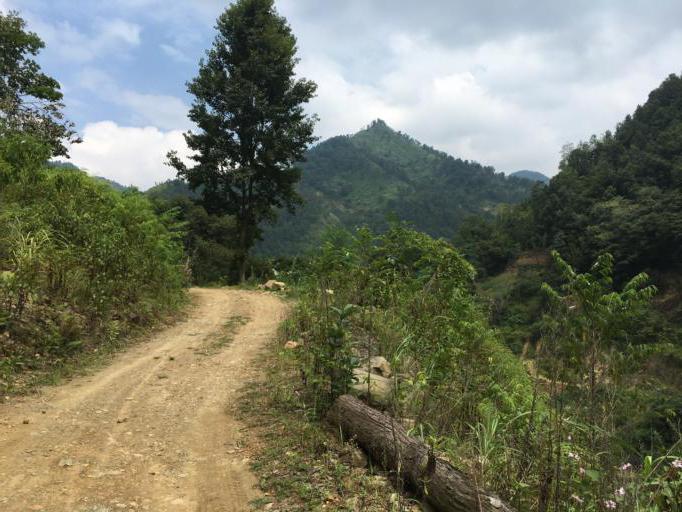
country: CN
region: Guangxi Zhuangzu Zizhiqu
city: Tongle
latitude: 25.2974
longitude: 106.1420
